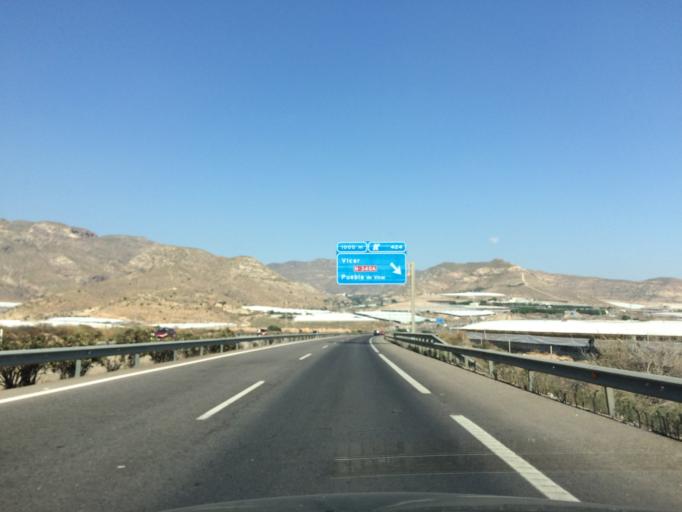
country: ES
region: Andalusia
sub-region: Provincia de Almeria
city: Vicar
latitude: 36.8089
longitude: -2.6678
